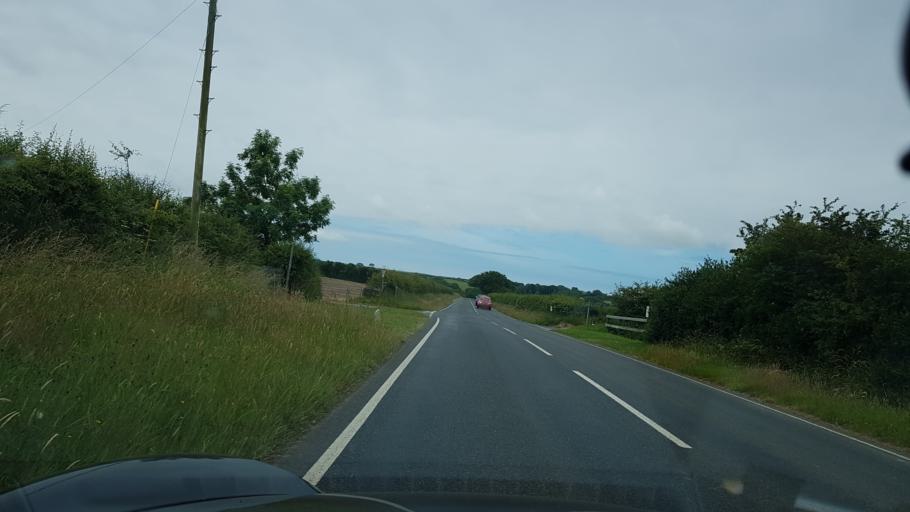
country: GB
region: Wales
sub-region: Pembrokeshire
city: Haverfordwest
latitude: 51.7951
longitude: -4.9955
